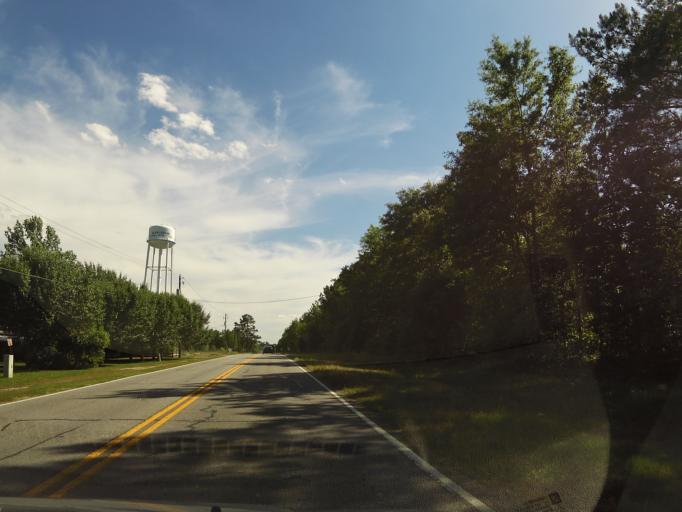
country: US
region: South Carolina
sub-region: Bamberg County
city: Denmark
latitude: 33.1877
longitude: -81.1826
